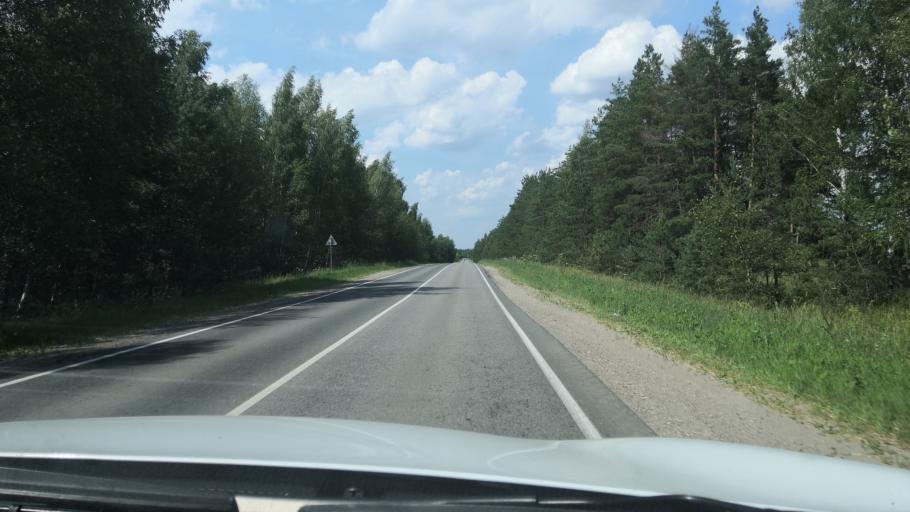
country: RU
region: Rjazan
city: Murmino
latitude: 54.5785
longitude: 40.1098
